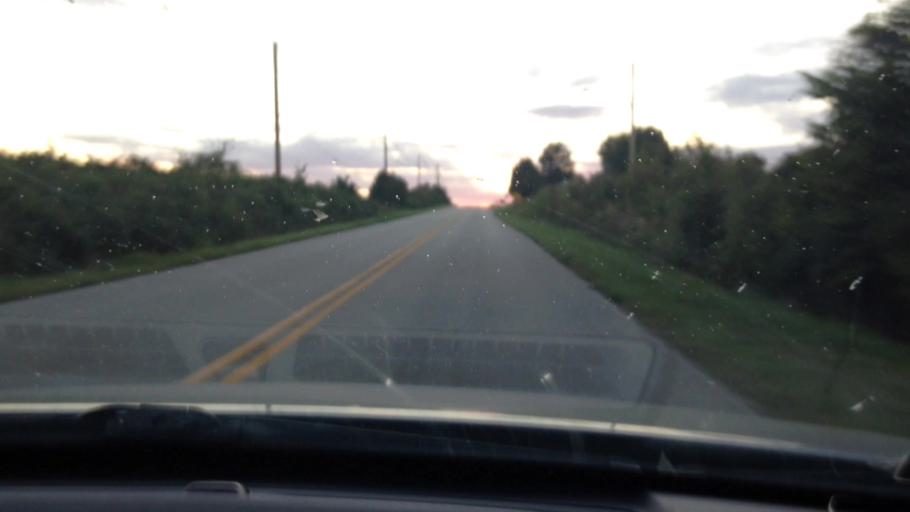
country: US
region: Kansas
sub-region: Leavenworth County
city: Lansing
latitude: 39.1870
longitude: -94.8551
